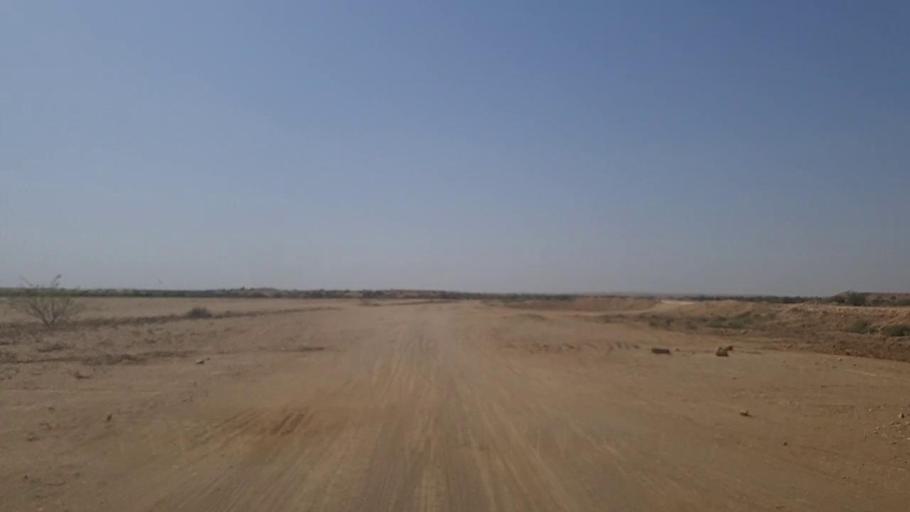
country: PK
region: Sindh
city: Kotri
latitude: 25.1487
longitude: 68.1631
